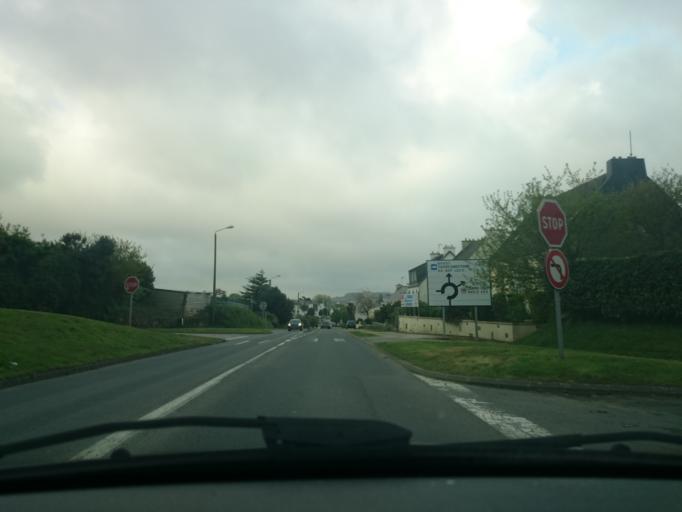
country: FR
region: Brittany
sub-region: Departement du Finistere
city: Saint-Renan
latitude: 48.4400
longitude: -4.6205
